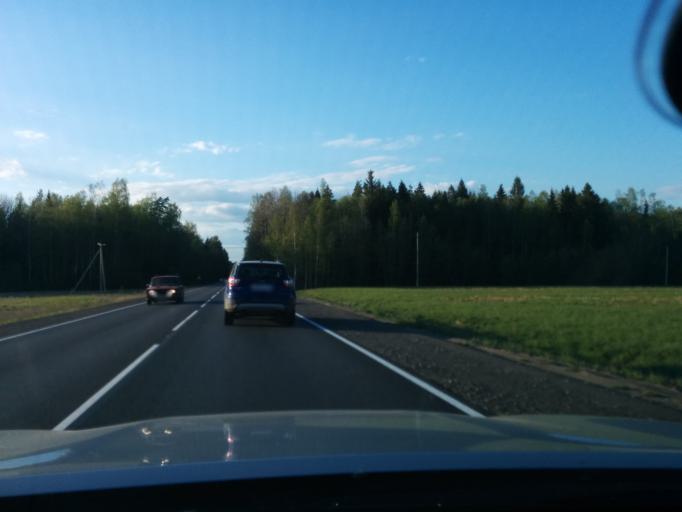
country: RU
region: Leningrad
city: Verkhniye Osel'ki
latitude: 60.2046
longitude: 30.4264
